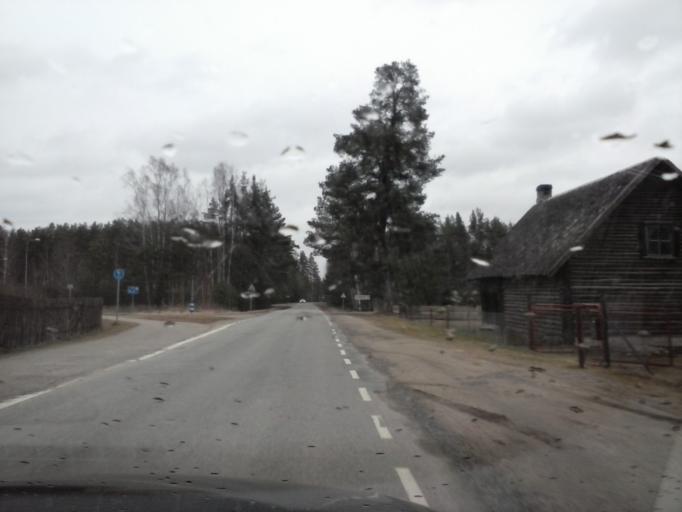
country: RU
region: Pskov
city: Pechory
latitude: 57.9608
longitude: 27.6293
